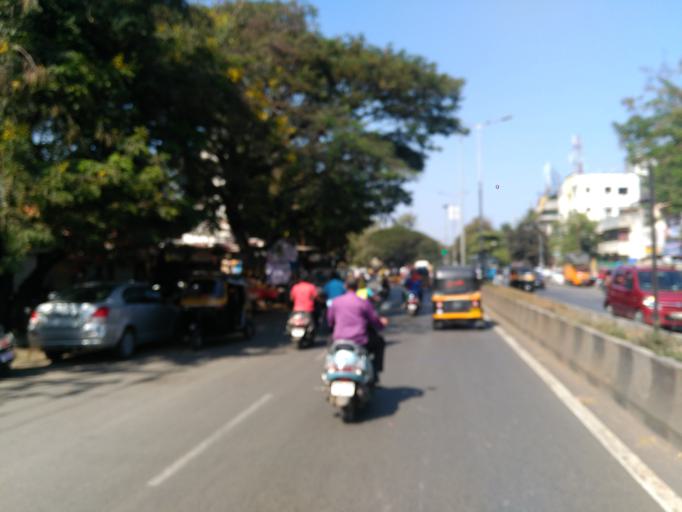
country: IN
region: Maharashtra
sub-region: Pune Division
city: Pune
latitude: 18.4679
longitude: 73.8643
